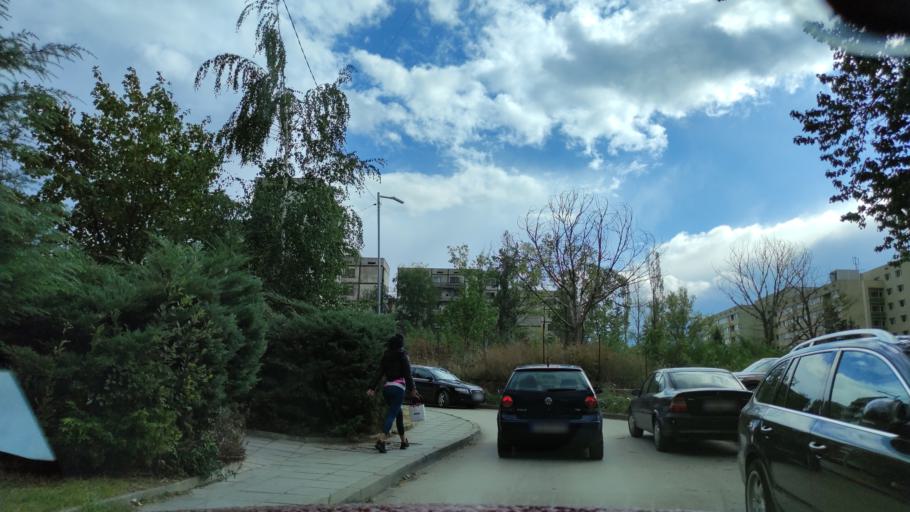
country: BG
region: Sofia-Capital
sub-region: Stolichna Obshtina
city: Sofia
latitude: 42.6562
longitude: 23.3431
